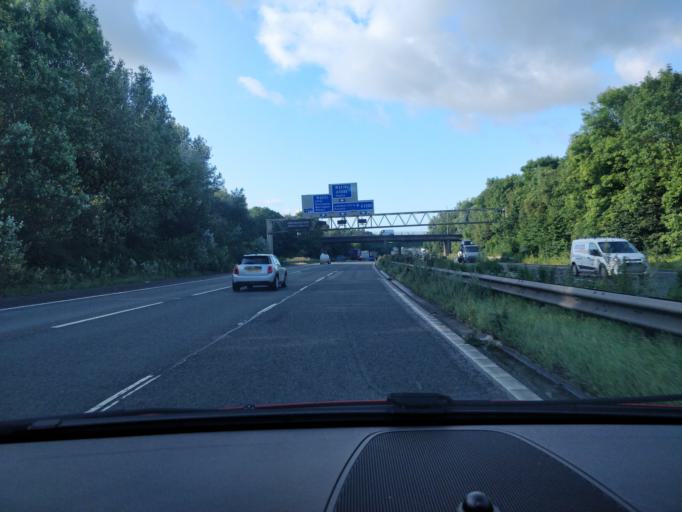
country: GB
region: England
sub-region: Knowsley
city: Prescot
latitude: 53.4151
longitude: -2.8129
